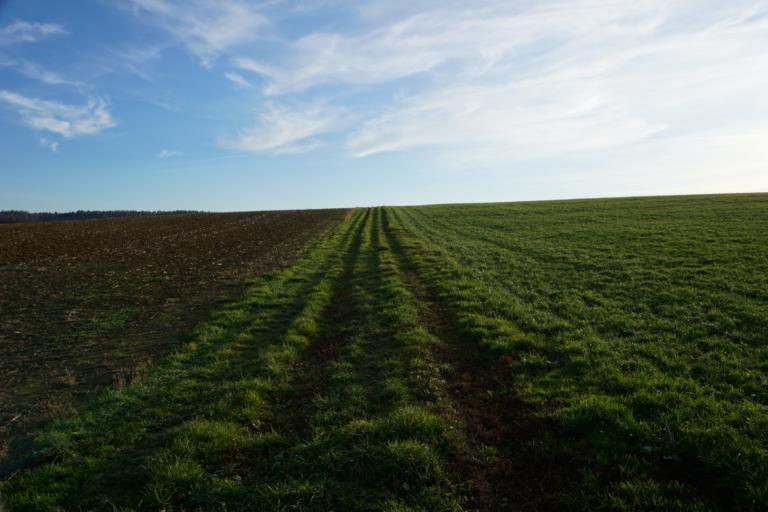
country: DE
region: Baden-Wuerttemberg
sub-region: Karlsruhe Region
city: Neunkirchen
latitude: 49.3733
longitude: 9.0222
